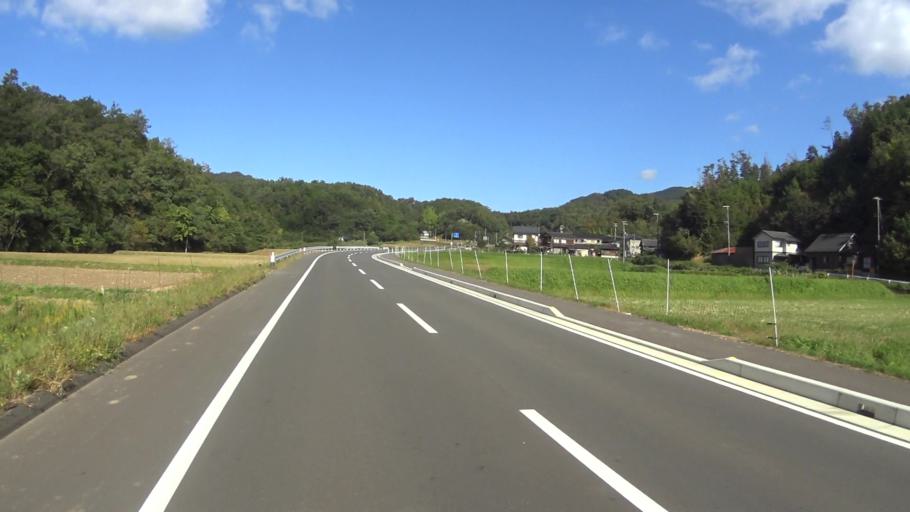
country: JP
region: Kyoto
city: Miyazu
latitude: 35.6135
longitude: 135.1319
